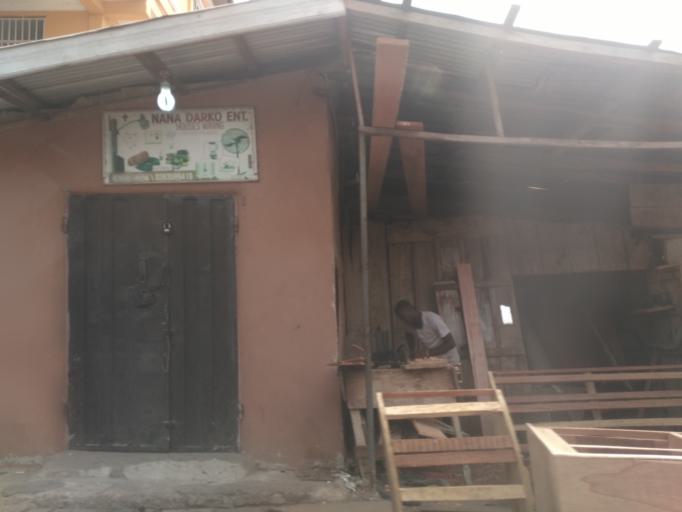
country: GH
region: Ashanti
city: Kumasi
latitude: 6.7037
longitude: -1.6097
